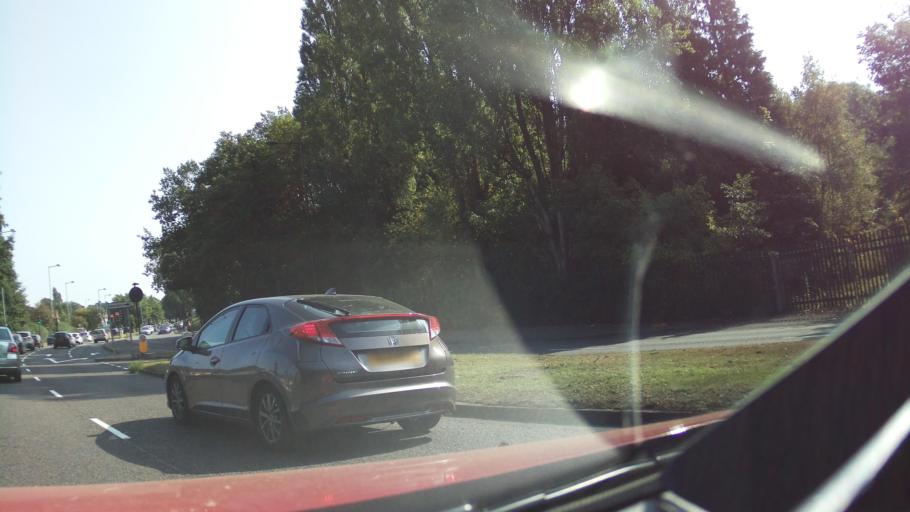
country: GB
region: England
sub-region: Walsall
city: Streetly
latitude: 52.5516
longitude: -1.9126
